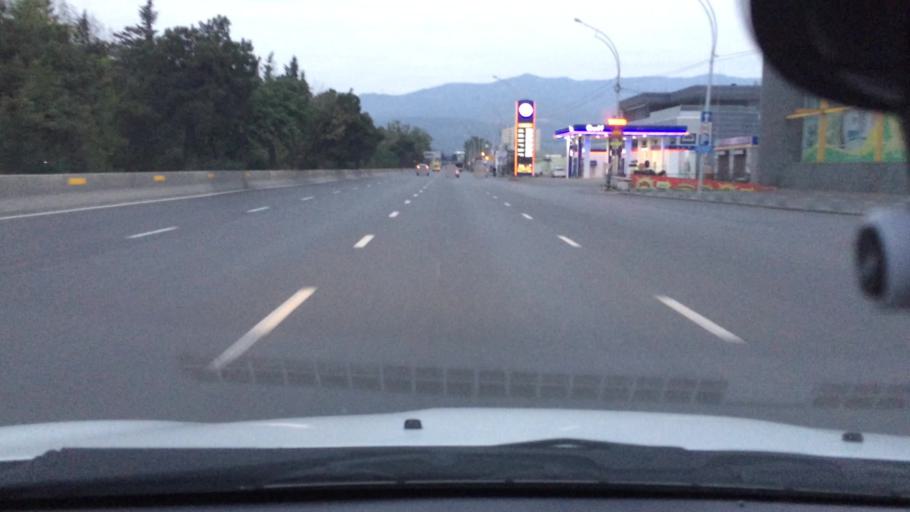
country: GE
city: Zahesi
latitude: 41.7881
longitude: 44.7702
